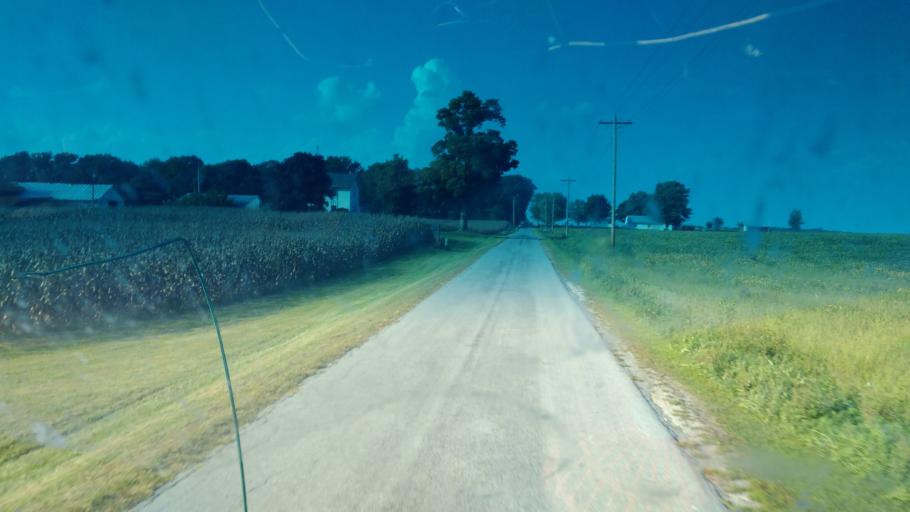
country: US
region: Ohio
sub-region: Wyandot County
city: Upper Sandusky
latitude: 40.9106
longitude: -83.1893
